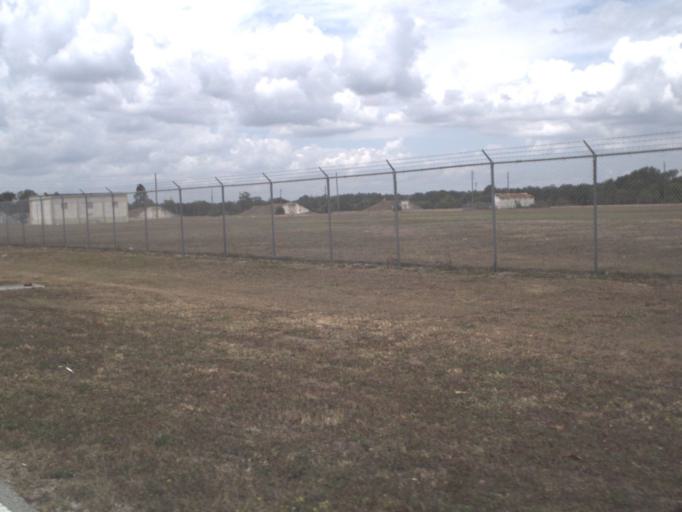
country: US
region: Florida
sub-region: Orange County
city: Taft
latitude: 28.4166
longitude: -81.3372
